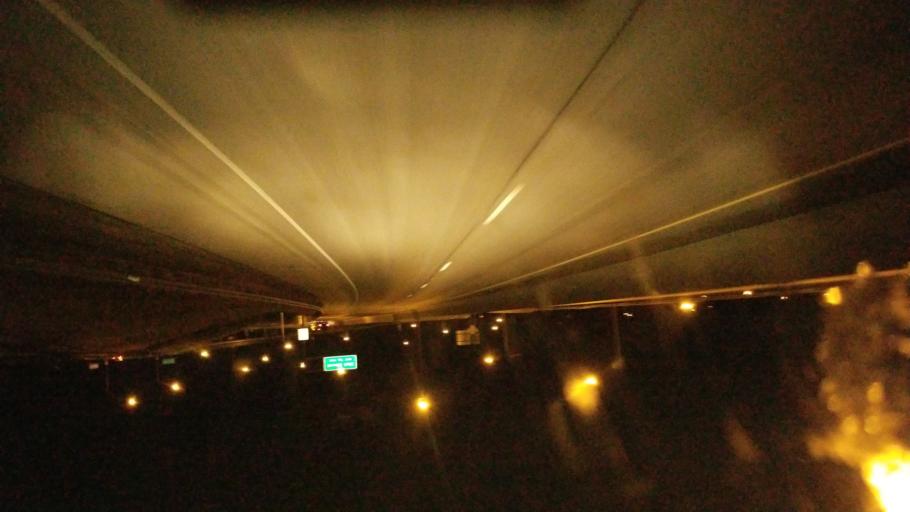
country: US
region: Ohio
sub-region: Licking County
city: Newark
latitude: 40.0599
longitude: -82.4157
